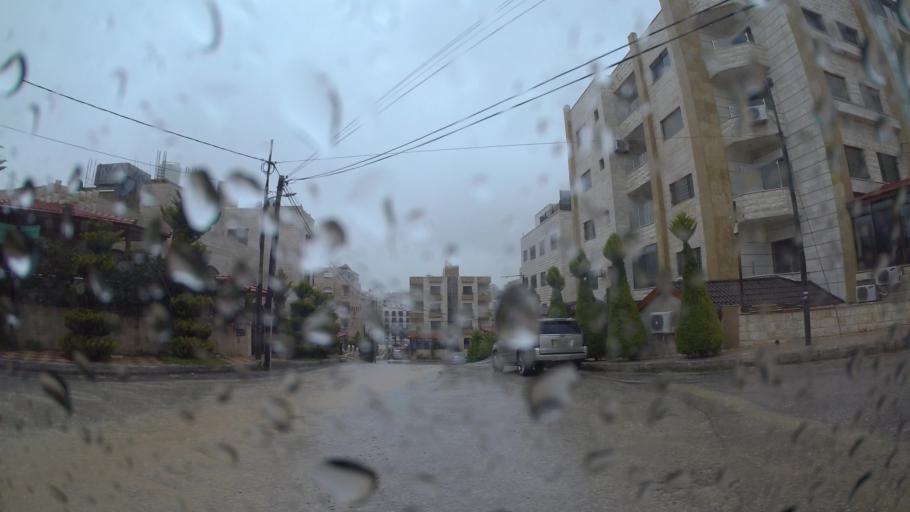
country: JO
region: Amman
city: Al Jubayhah
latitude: 32.0222
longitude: 35.8918
